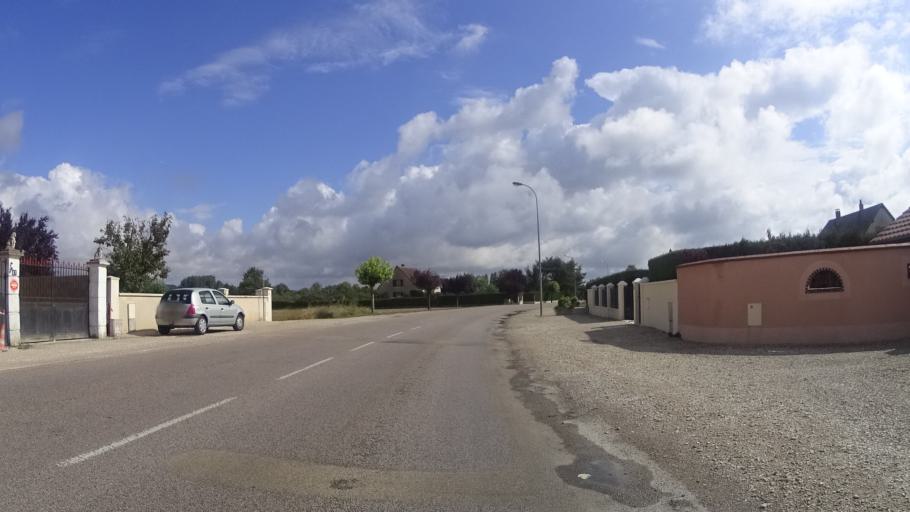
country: FR
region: Bourgogne
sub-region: Departement de l'Yonne
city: Vergigny
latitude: 47.9773
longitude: 3.7246
